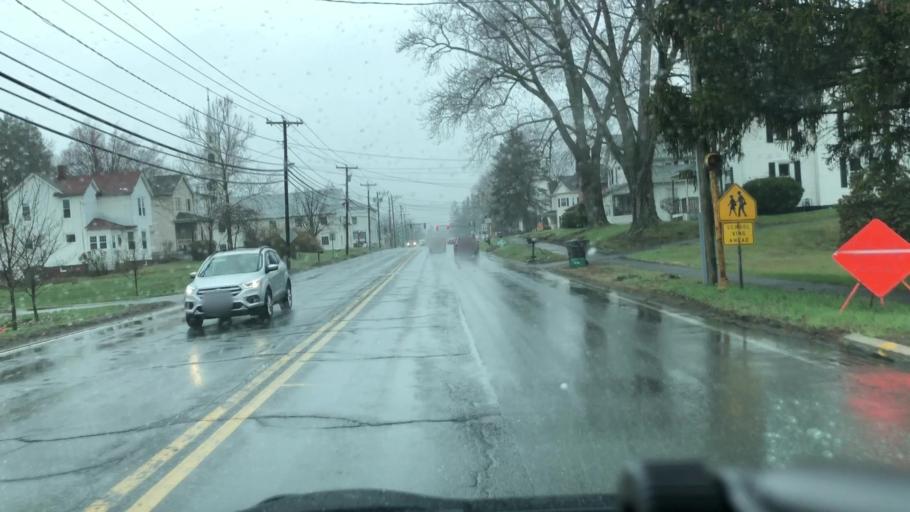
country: US
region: Massachusetts
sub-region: Hampshire County
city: Hadley
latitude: 42.3424
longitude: -72.5864
